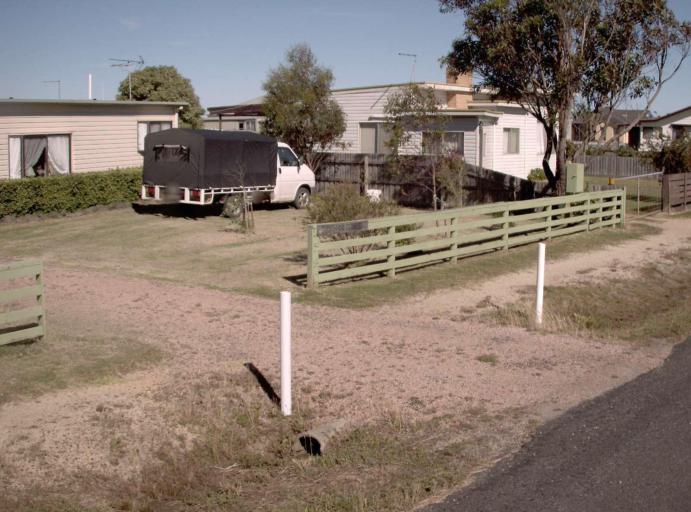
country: AU
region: Victoria
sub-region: Latrobe
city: Traralgon
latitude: -38.6671
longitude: 146.6897
